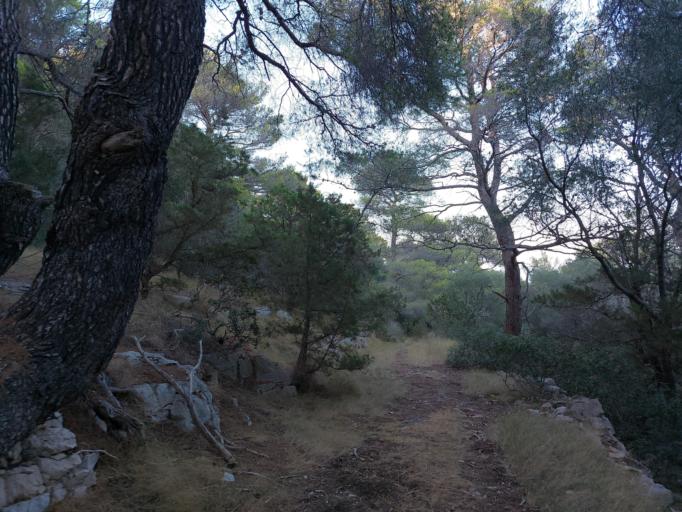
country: HR
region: Dubrovacko-Neretvanska
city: Smokvica
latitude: 42.7710
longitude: 16.7903
